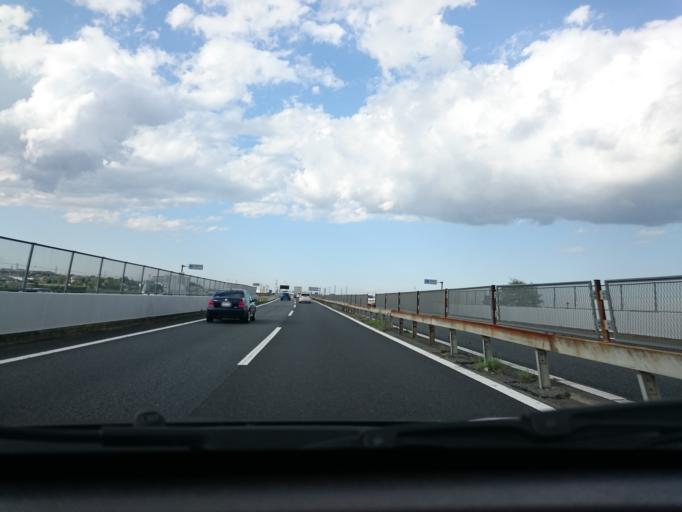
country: JP
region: Kanagawa
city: Isehara
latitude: 35.3805
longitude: 139.3292
